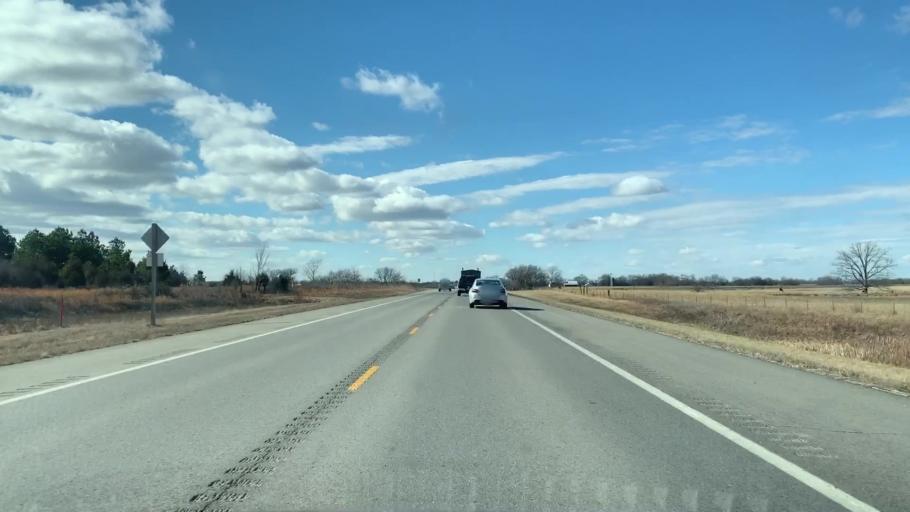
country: US
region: Kansas
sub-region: Crawford County
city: Pittsburg
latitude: 37.3396
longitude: -94.8457
